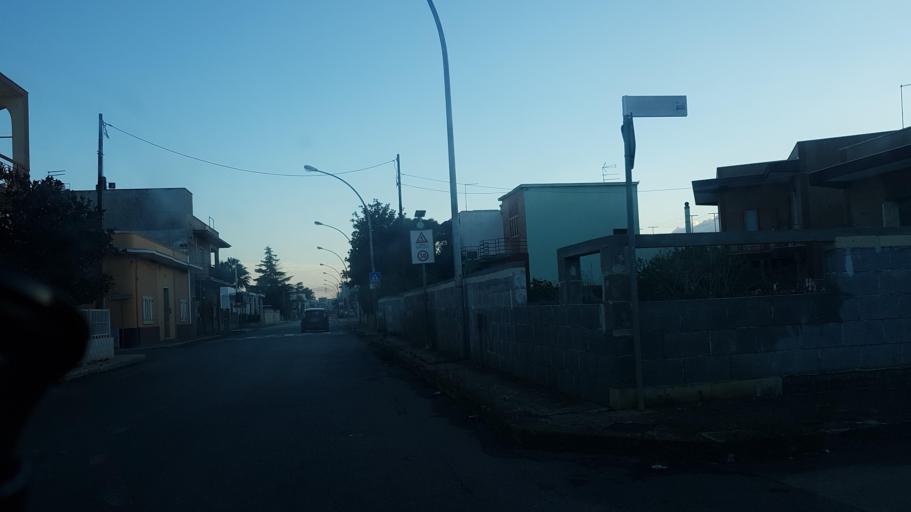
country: IT
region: Apulia
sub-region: Provincia di Brindisi
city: San Michele Salentino
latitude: 40.6364
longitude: 17.6321
